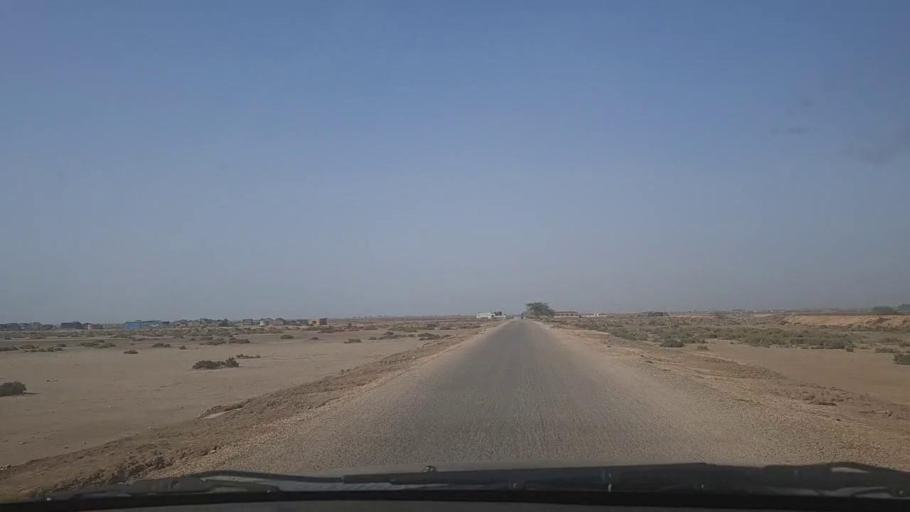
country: PK
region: Sindh
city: Keti Bandar
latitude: 24.1784
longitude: 67.5164
